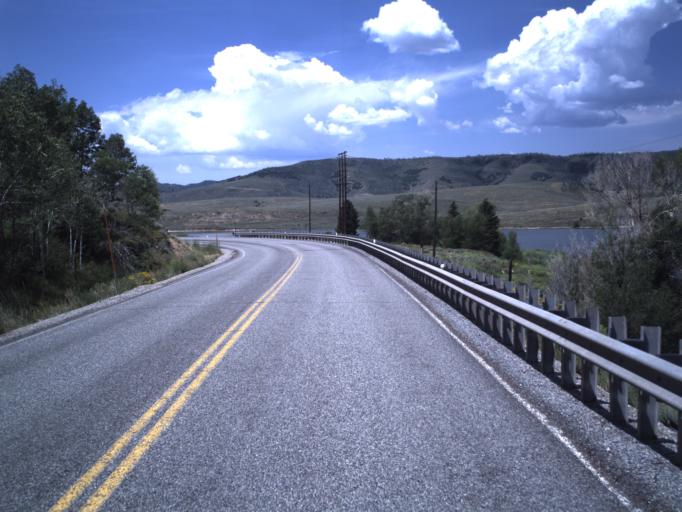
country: US
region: Utah
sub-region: Carbon County
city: Helper
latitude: 39.7872
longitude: -111.1302
